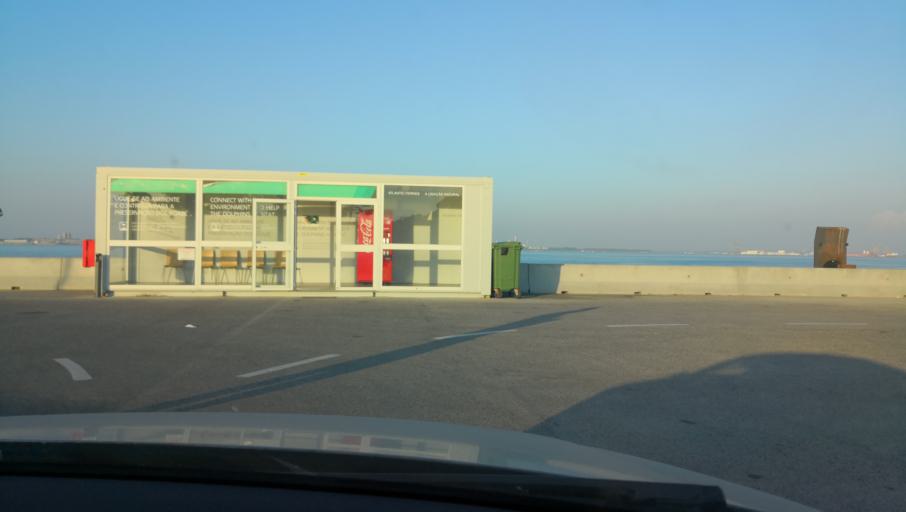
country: PT
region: Setubal
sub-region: Setubal
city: Setubal
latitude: 38.4670
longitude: -8.8628
